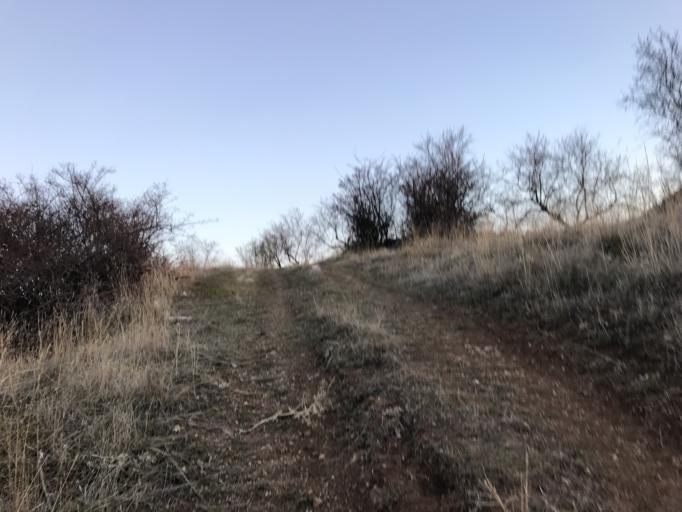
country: ES
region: Andalusia
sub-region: Provincia de Granada
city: Beas de Granada
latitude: 37.2211
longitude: -3.4673
